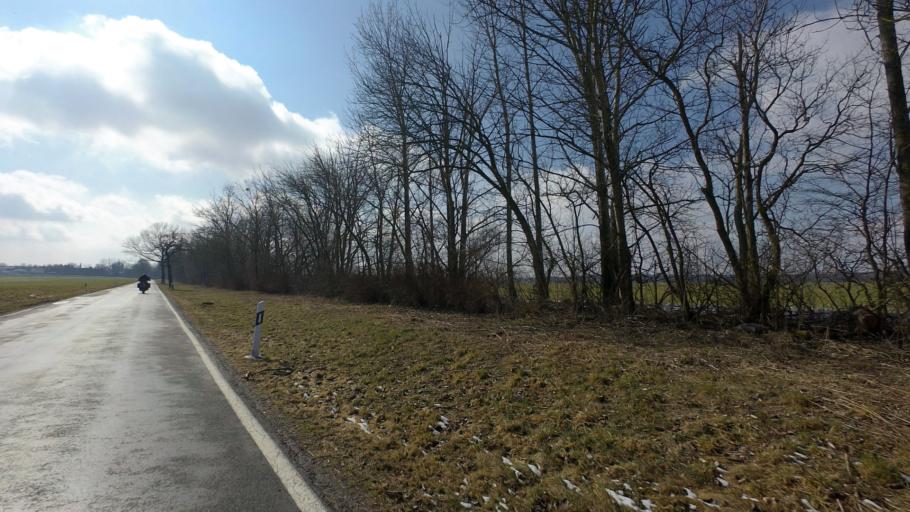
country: DE
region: Brandenburg
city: Werneuchen
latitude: 52.6905
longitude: 13.7265
